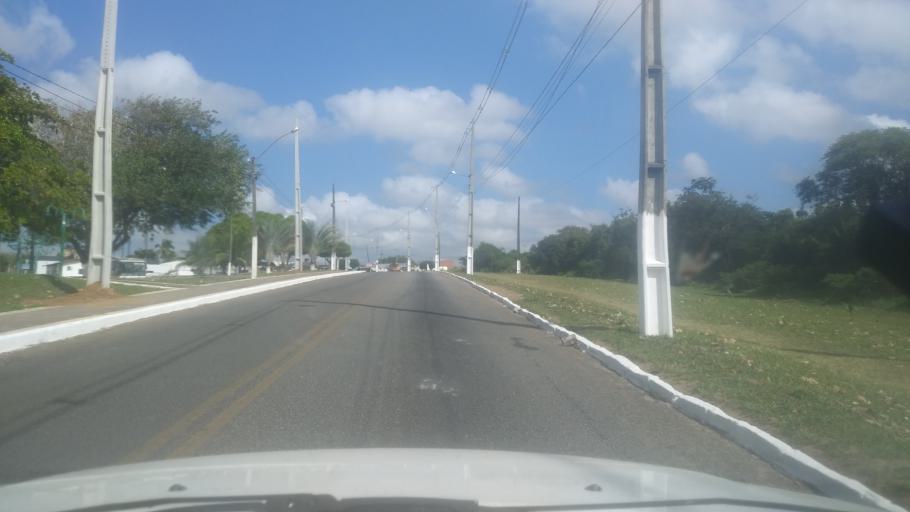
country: BR
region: Rio Grande do Norte
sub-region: Extremoz
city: Extremoz
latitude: -5.7040
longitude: -35.2869
